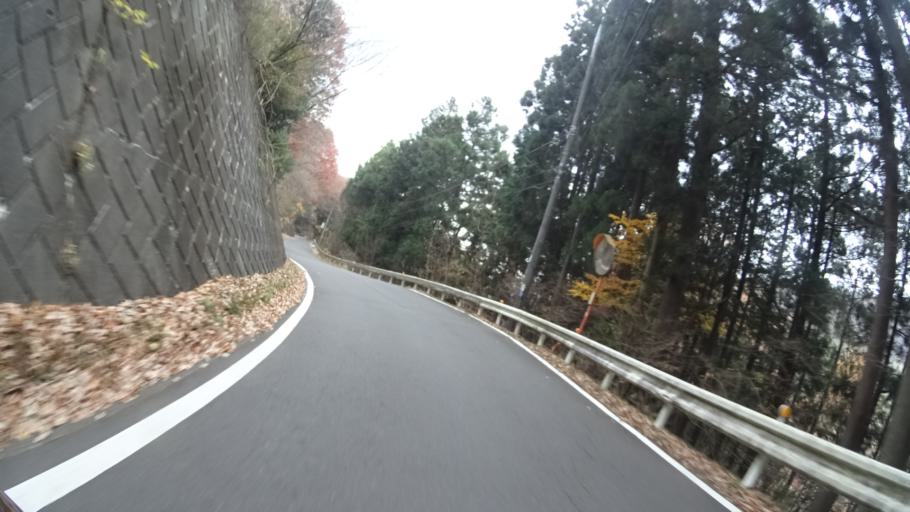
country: JP
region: Gunma
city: Omamacho-omama
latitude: 36.4935
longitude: 139.1841
